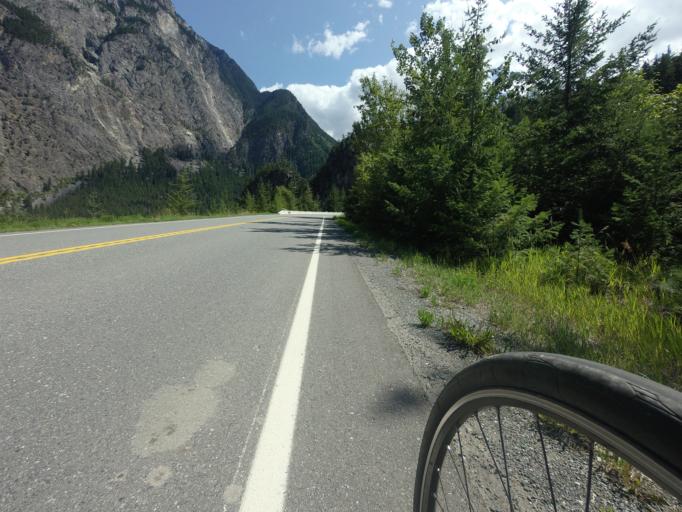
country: CA
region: British Columbia
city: Lillooet
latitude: 50.6620
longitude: -121.9871
